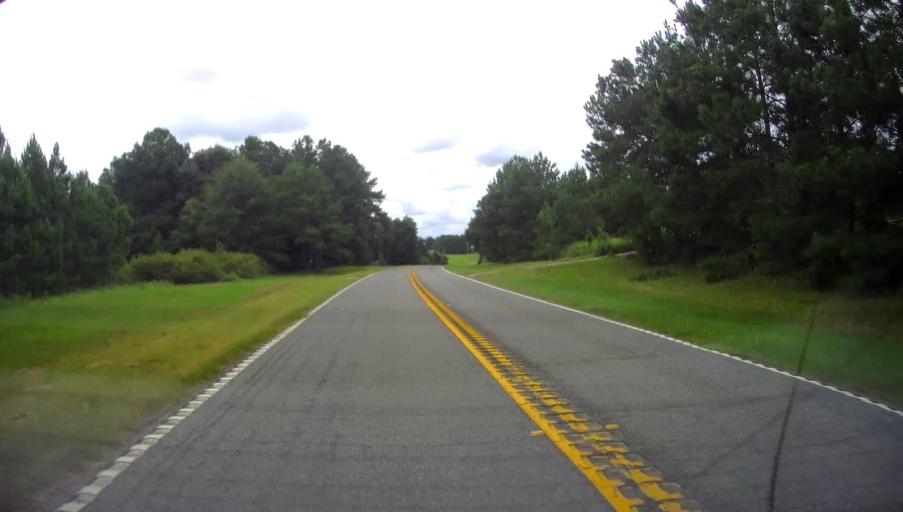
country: US
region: Georgia
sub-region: Dooly County
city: Unadilla
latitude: 32.2823
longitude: -83.8228
